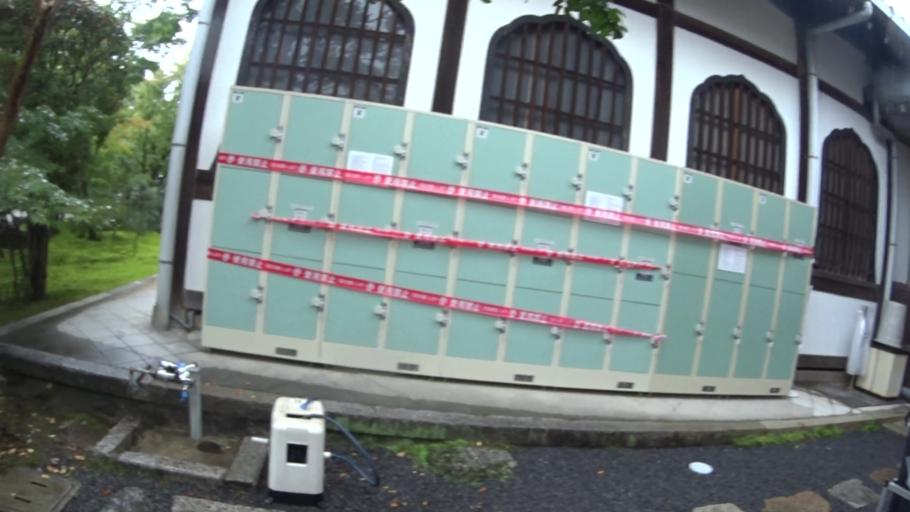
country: JP
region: Shiga Prefecture
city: Otsu-shi
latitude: 34.9843
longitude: 135.8101
